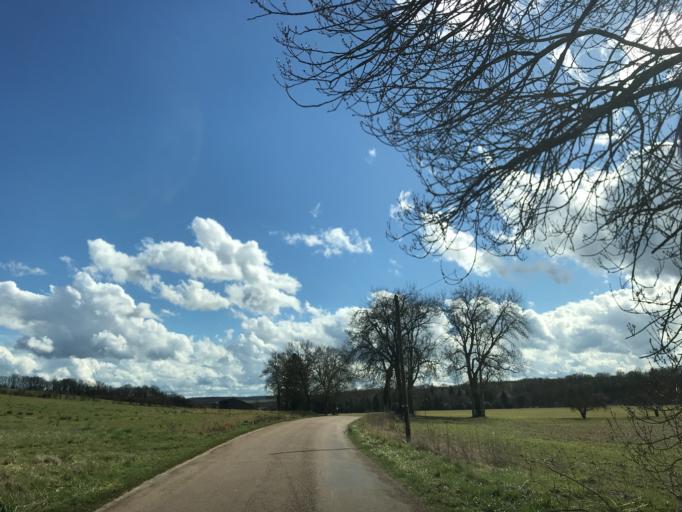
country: FR
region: Bourgogne
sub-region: Departement de l'Yonne
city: Fontenailles
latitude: 47.5160
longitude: 3.4943
